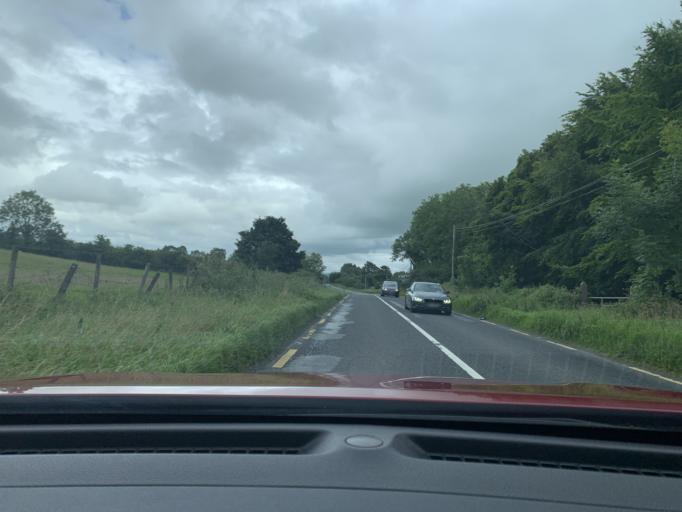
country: IE
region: Ulster
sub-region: County Donegal
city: Convoy
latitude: 54.8008
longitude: -7.6266
